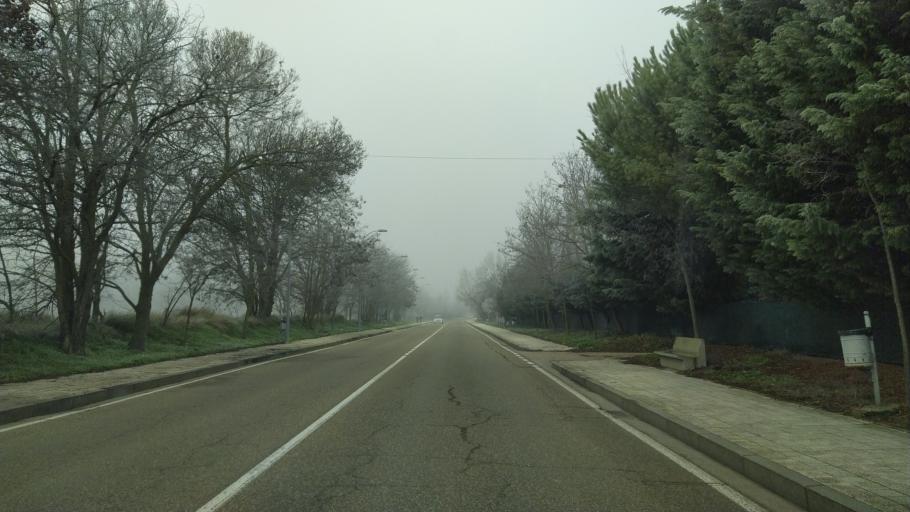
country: ES
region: Castille and Leon
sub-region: Provincia de Palencia
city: Palencia
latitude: 41.9955
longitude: -4.5368
